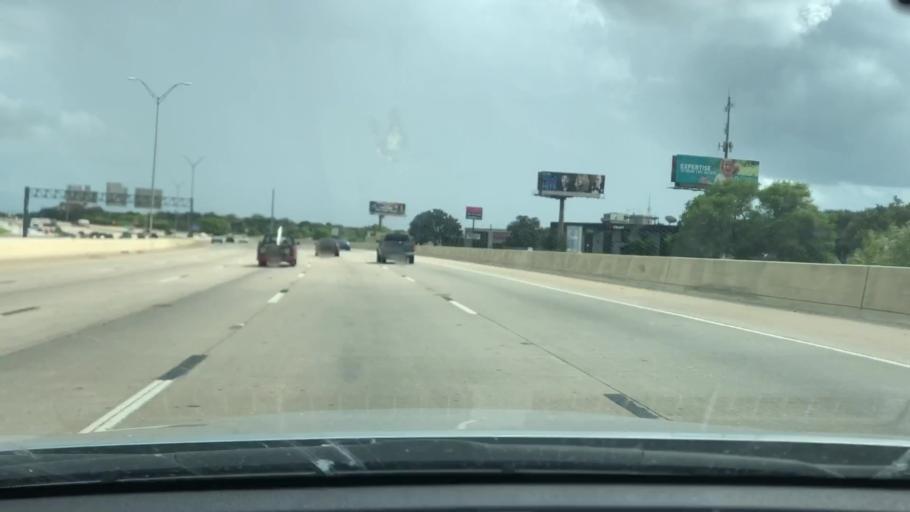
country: US
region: Texas
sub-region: Bexar County
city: Balcones Heights
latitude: 29.4866
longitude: -98.5436
